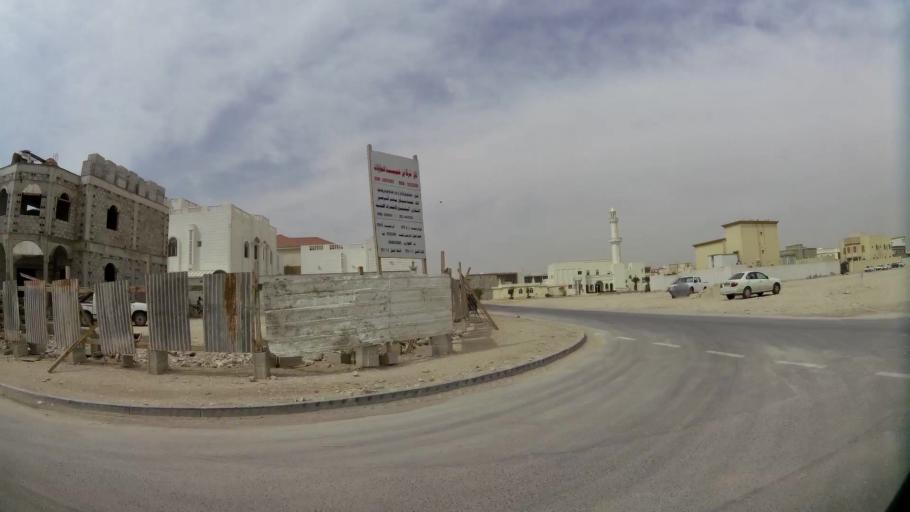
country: QA
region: Al Wakrah
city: Al Wukayr
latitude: 25.1977
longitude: 51.4574
